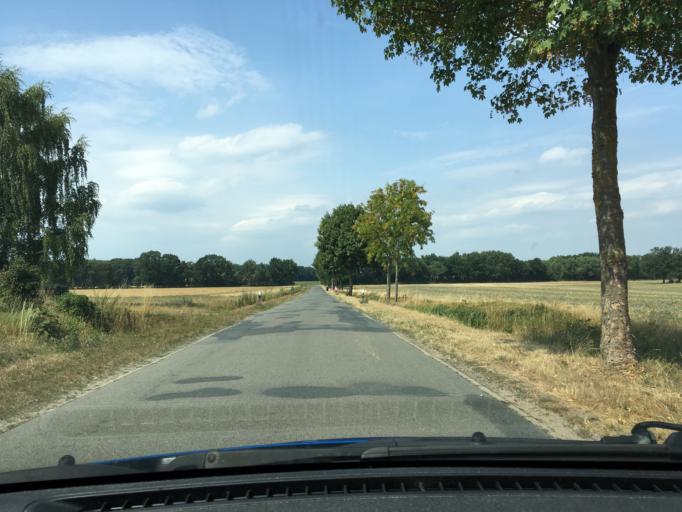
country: DE
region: Lower Saxony
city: Natendorf
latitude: 53.1138
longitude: 10.4456
